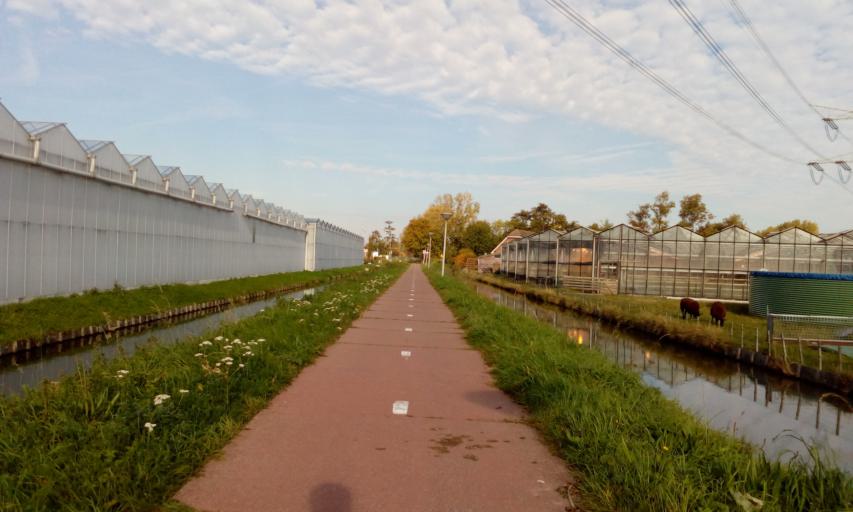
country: NL
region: South Holland
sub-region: Gemeente Westland
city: Naaldwijk
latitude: 51.9773
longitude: 4.2154
